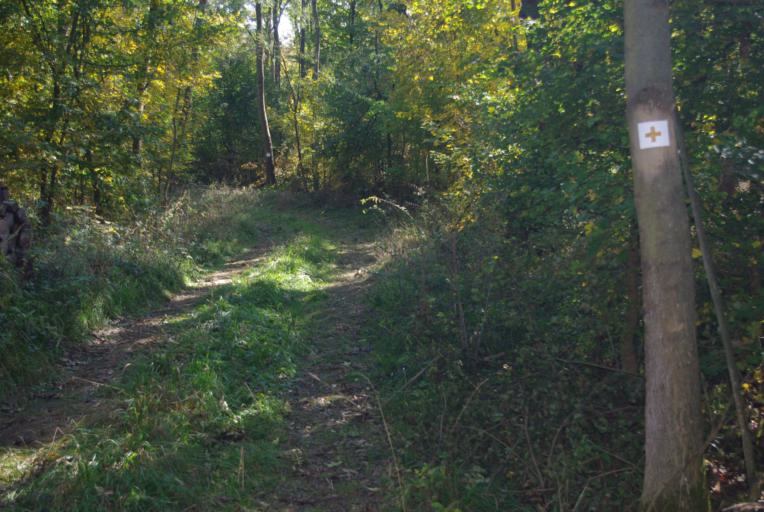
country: HU
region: Pest
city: Budakeszi
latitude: 47.5399
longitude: 18.8994
